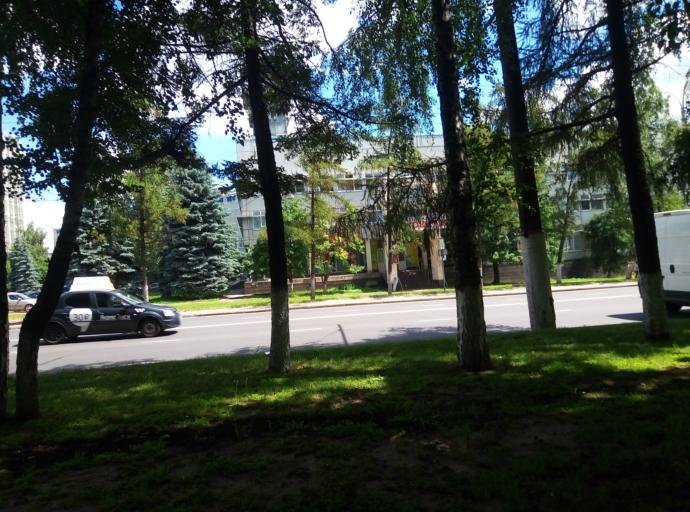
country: RU
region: Kursk
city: Kursk
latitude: 51.7559
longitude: 36.1886
